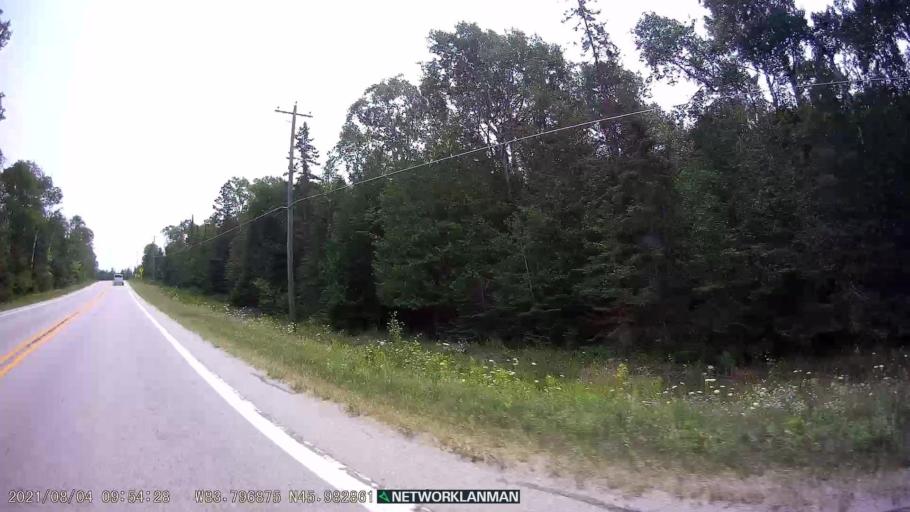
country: CA
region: Ontario
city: Thessalon
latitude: 45.9828
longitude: -83.7968
